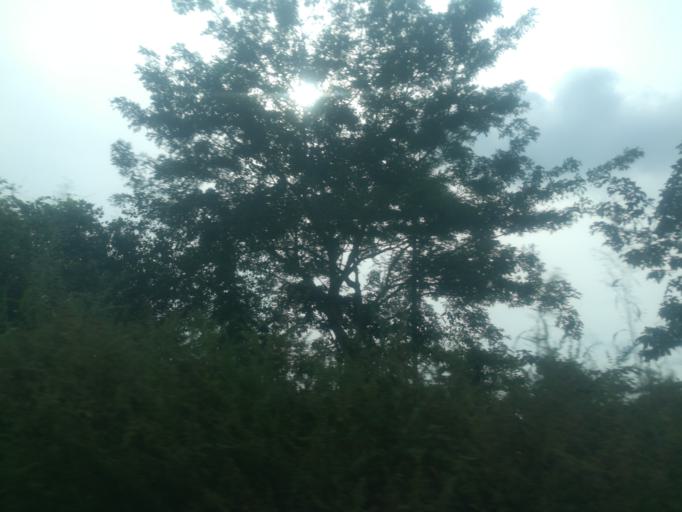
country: NG
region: Ogun
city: Ayetoro
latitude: 7.2999
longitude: 3.0761
